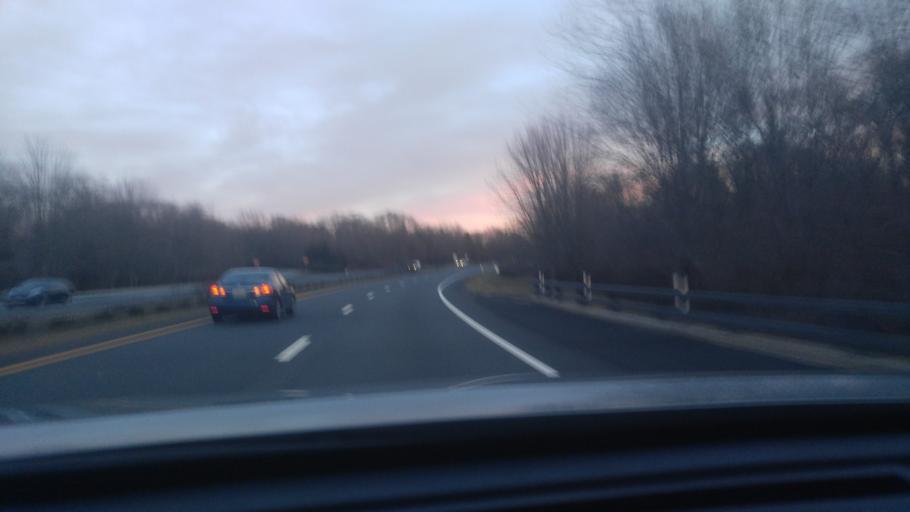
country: US
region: Rhode Island
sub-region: Newport County
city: Jamestown
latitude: 41.5259
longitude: -71.3713
